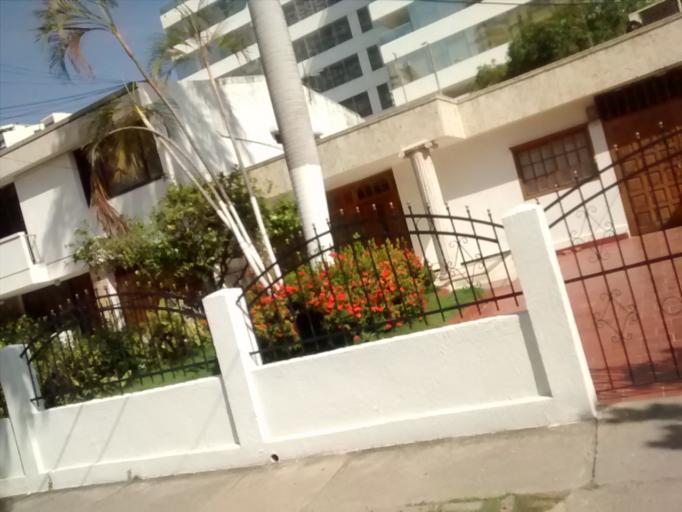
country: CO
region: Bolivar
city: Cartagena
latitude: 10.4003
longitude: -75.5555
